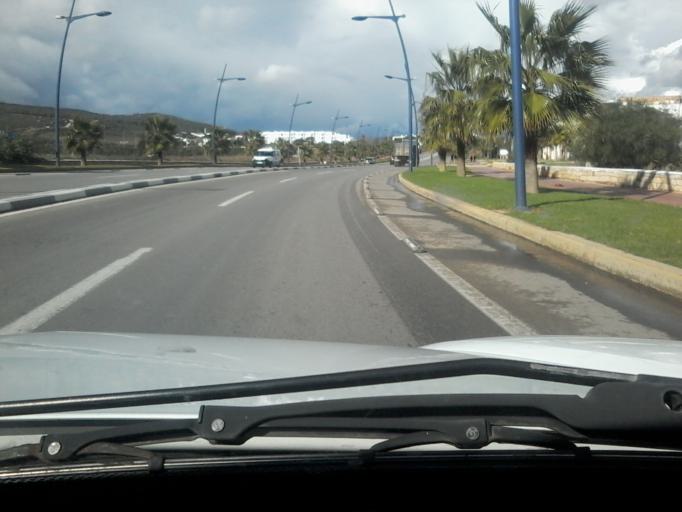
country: MA
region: Tanger-Tetouan
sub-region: Tetouan
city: Martil
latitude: 35.7447
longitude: -5.3452
